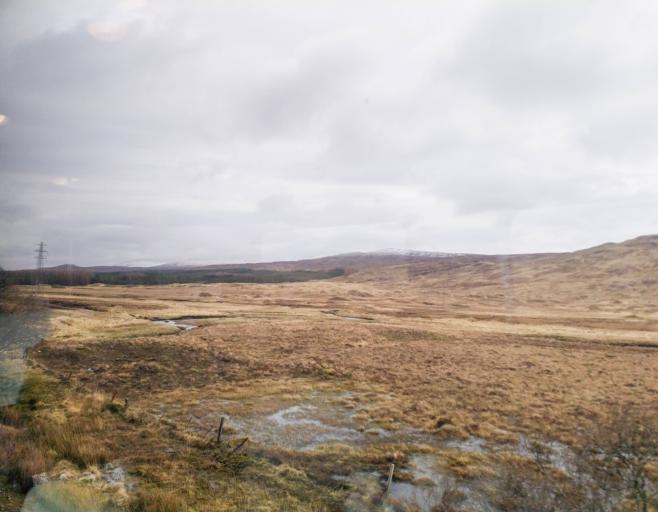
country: GB
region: Scotland
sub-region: Highland
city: Spean Bridge
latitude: 56.5996
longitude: -4.6085
